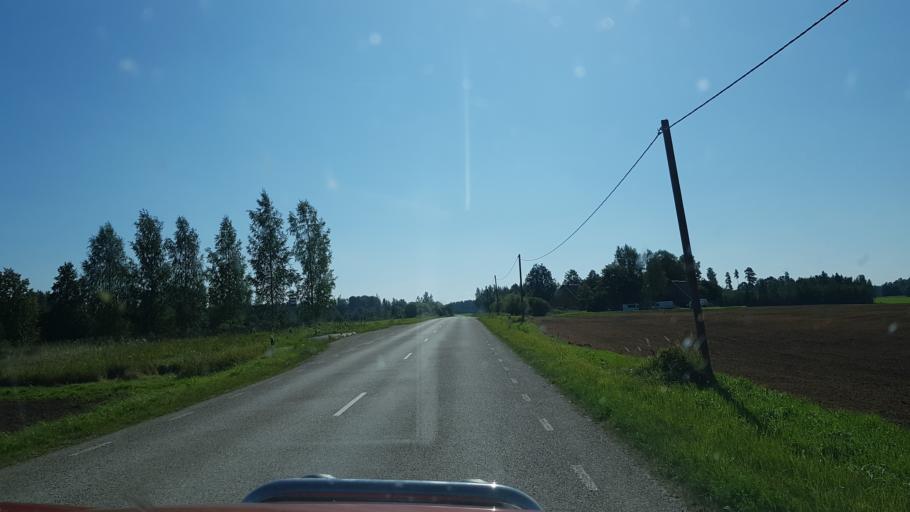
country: EE
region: Polvamaa
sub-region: Polva linn
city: Polva
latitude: 58.2286
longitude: 27.2248
